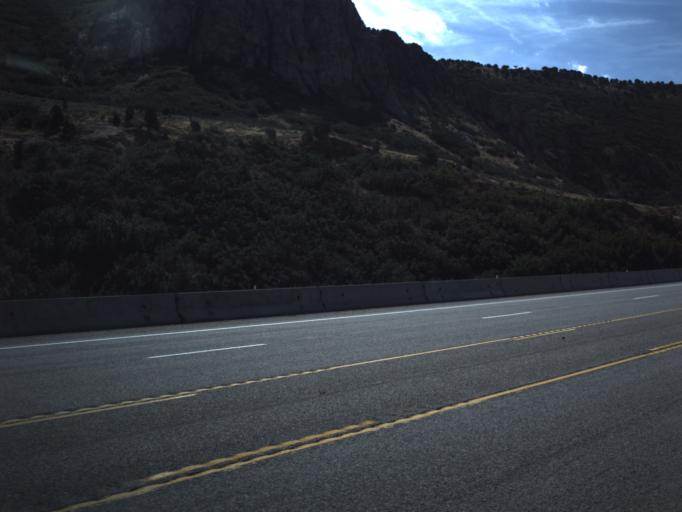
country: US
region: Utah
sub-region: Utah County
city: Mapleton
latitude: 40.0193
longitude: -111.4966
